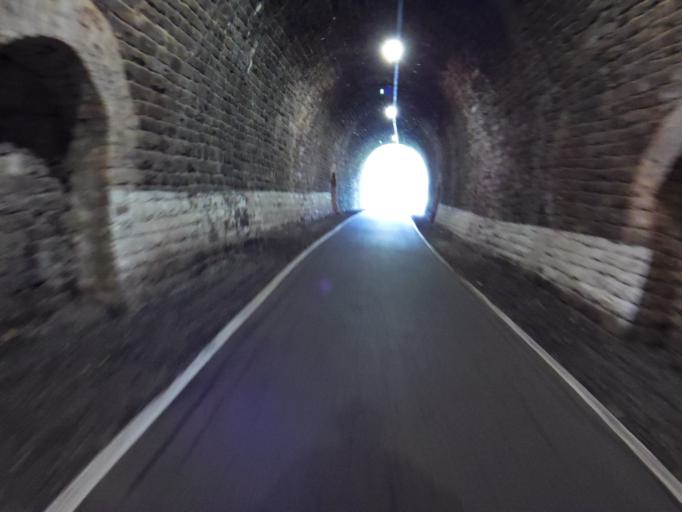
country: BE
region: Wallonia
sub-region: Province de Liege
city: Saint-Vith
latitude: 50.2363
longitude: 6.1560
